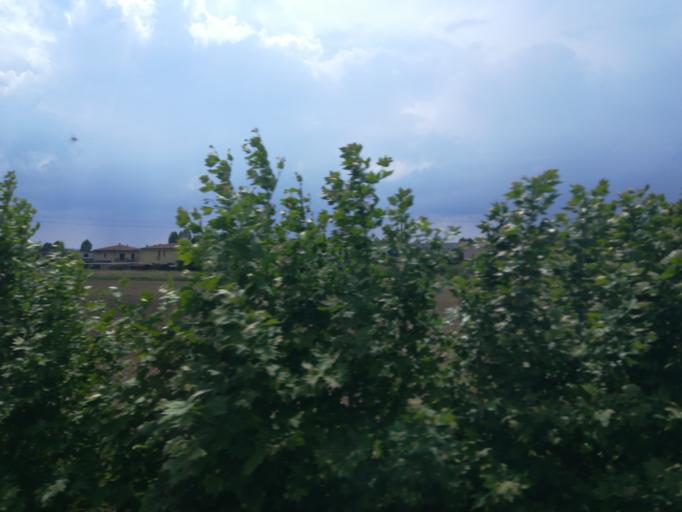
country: IT
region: Veneto
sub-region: Provincia di Vicenza
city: Dueville
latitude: 45.6259
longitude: 11.5561
